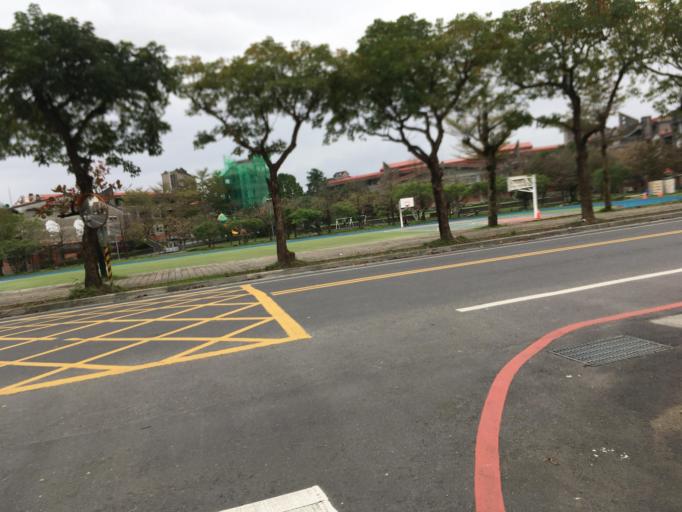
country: TW
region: Taiwan
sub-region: Yilan
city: Yilan
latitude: 24.6315
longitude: 121.7912
